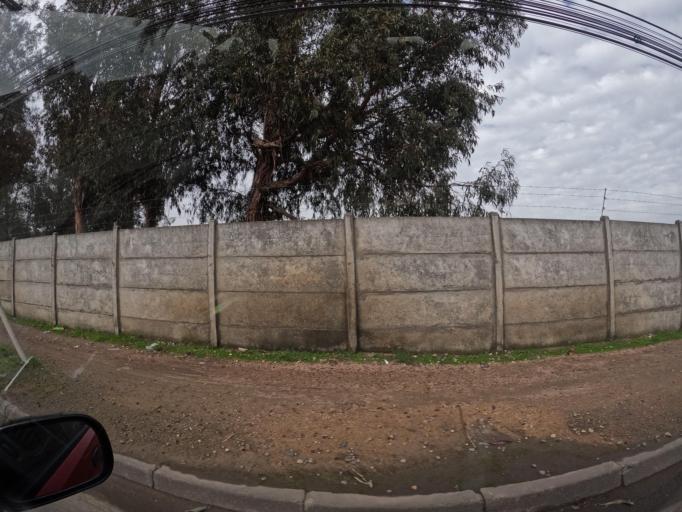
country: CL
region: Maule
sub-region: Provincia de Linares
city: Linares
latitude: -35.8389
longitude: -71.5945
